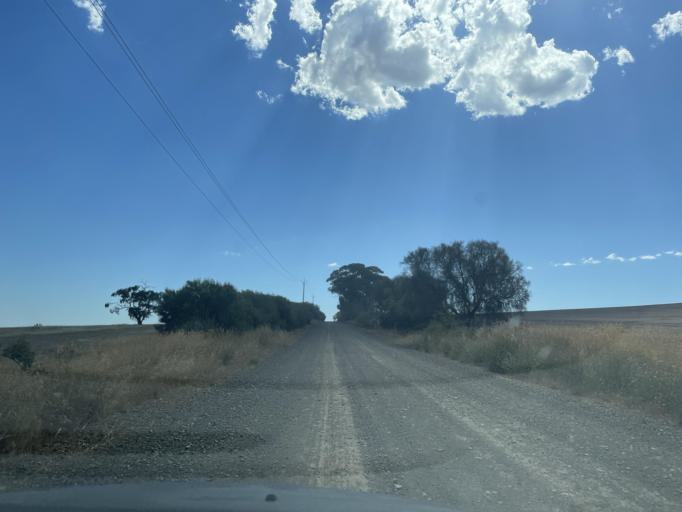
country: AU
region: South Australia
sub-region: Clare and Gilbert Valleys
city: Clare
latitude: -33.9094
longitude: 138.7340
